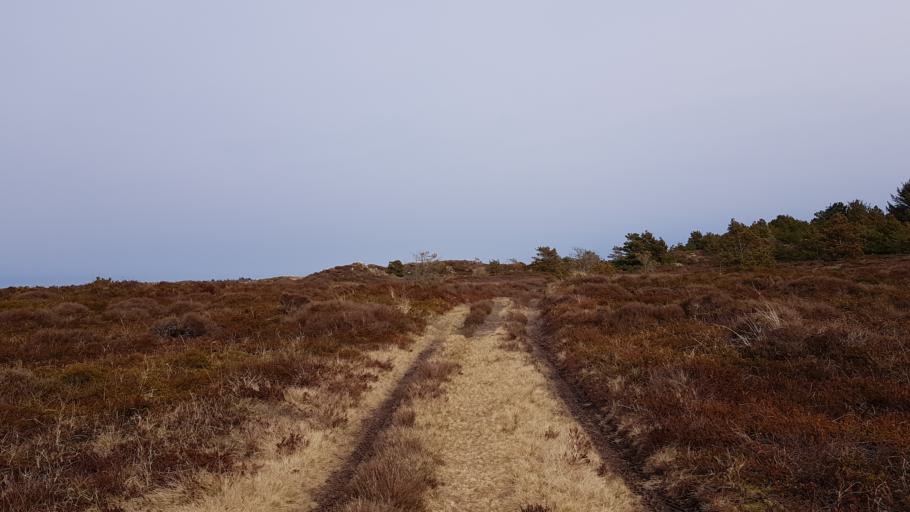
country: DE
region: Schleswig-Holstein
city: List
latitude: 55.1625
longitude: 8.5230
